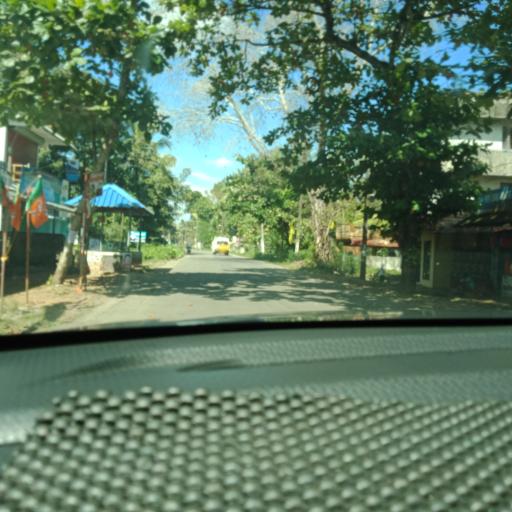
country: IN
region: Kerala
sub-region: Alappuzha
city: Mavelikara
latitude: 9.3063
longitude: 76.4562
